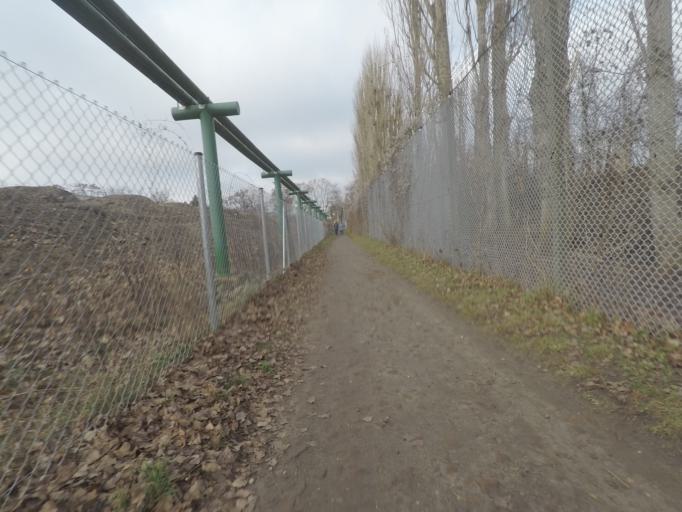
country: DE
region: Berlin
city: Mariendorf
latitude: 52.4439
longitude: 13.3637
